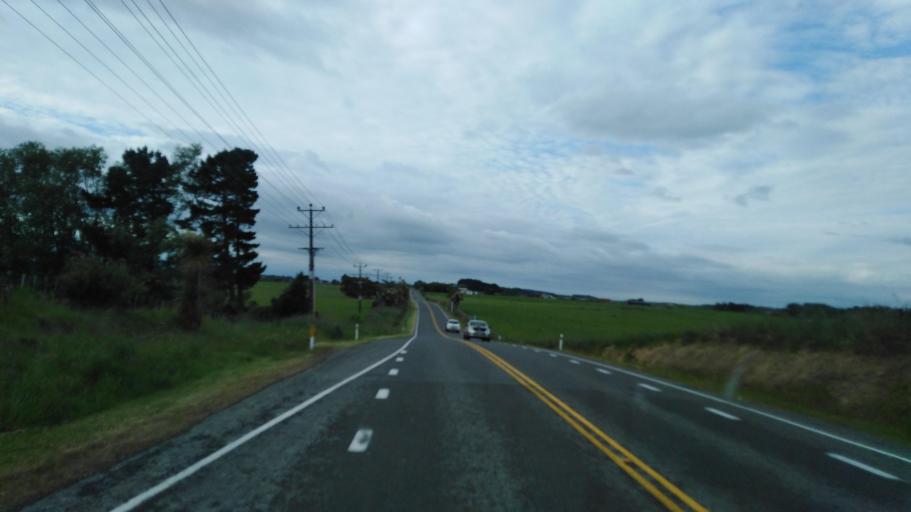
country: NZ
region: Manawatu-Wanganui
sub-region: Rangitikei District
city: Bulls
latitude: -40.1105
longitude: 175.3589
